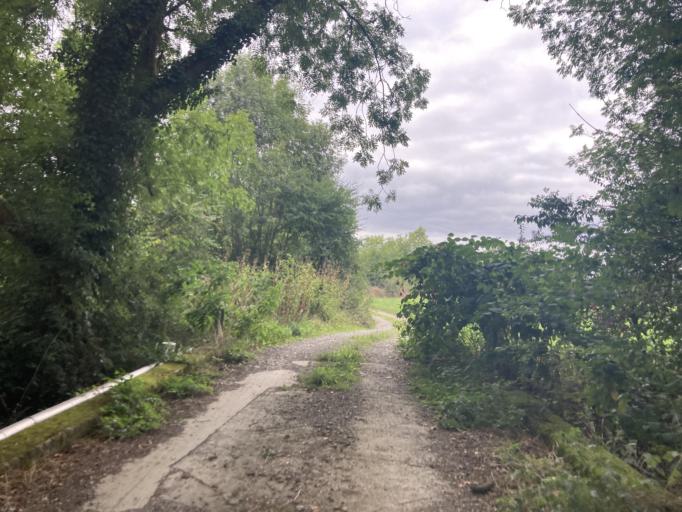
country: FR
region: Aquitaine
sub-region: Departement des Pyrenees-Atlantiques
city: Arbus
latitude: 43.3267
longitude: -0.4846
